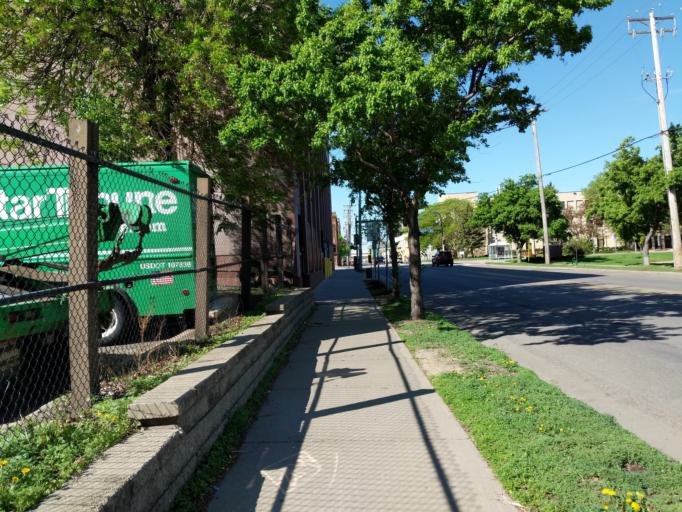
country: US
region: Minnesota
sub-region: Hennepin County
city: Minneapolis
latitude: 44.9908
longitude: -93.2797
